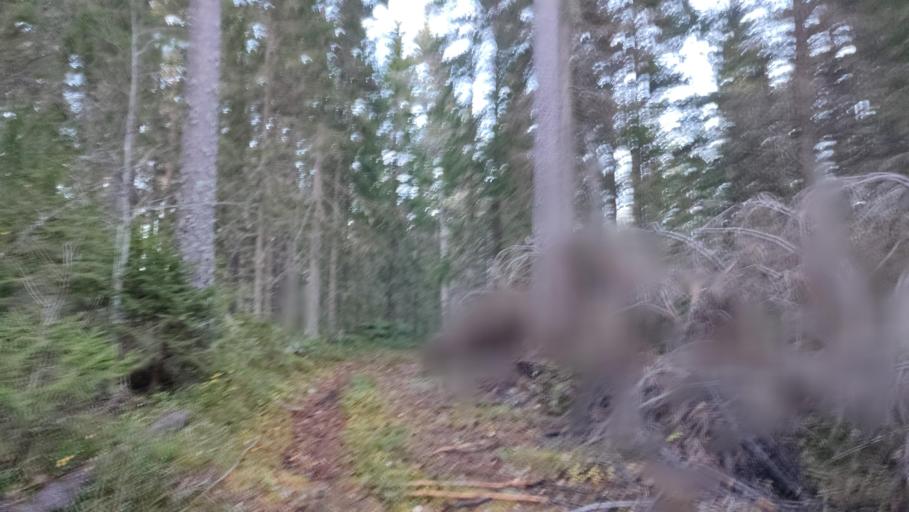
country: FI
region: Southern Ostrobothnia
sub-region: Suupohja
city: Karijoki
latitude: 62.2752
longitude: 21.6343
